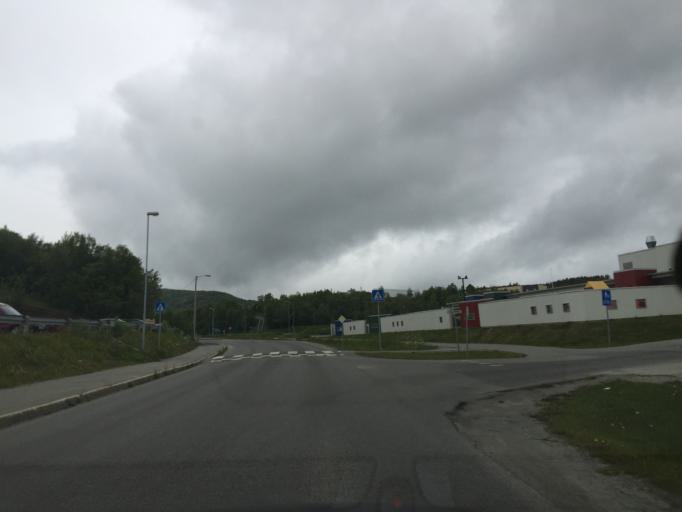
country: NO
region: Nordland
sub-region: Bodo
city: Lopsmarka
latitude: 67.2884
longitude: 14.5686
